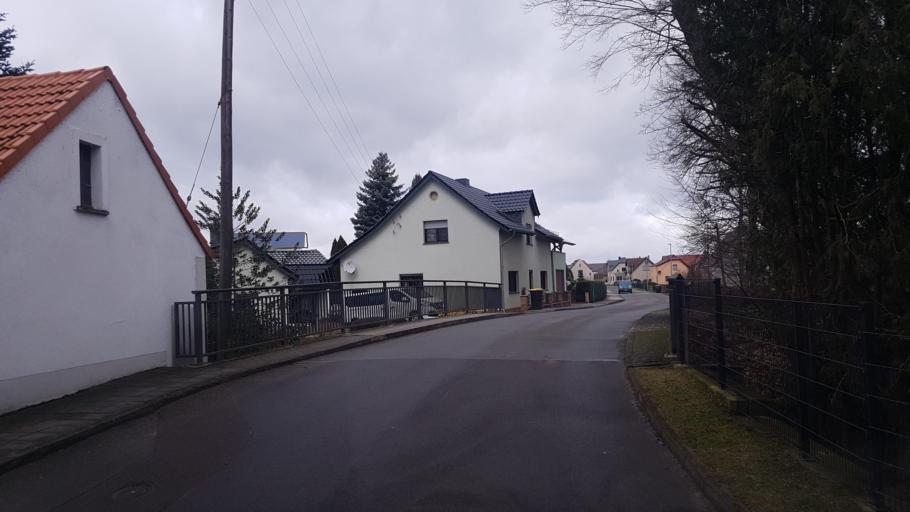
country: DE
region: Brandenburg
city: Kroppen
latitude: 51.3805
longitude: 13.7948
